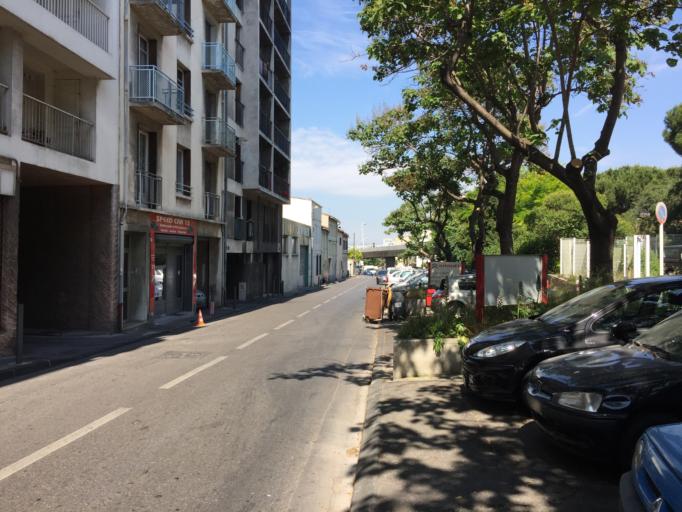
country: FR
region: Provence-Alpes-Cote d'Azur
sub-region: Departement des Bouches-du-Rhone
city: Marseille 04
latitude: 43.3145
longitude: 5.3924
